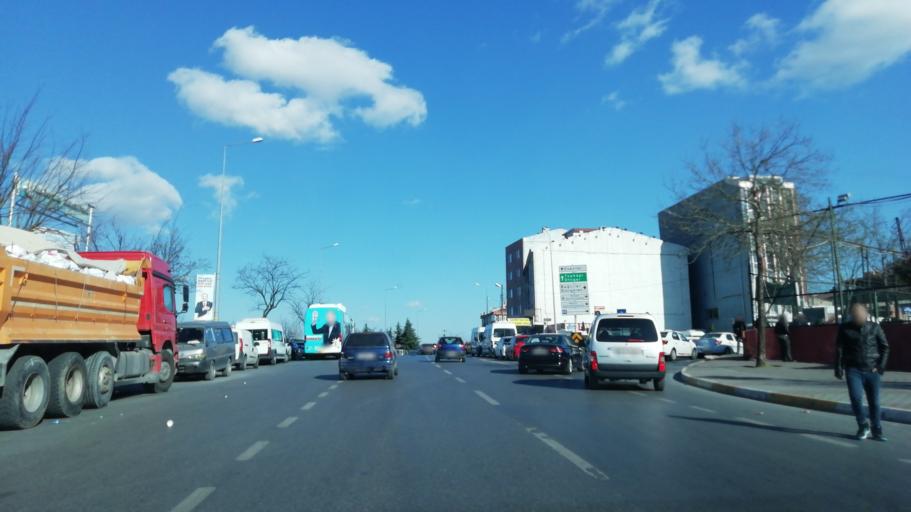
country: TR
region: Istanbul
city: Bagcilar
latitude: 41.0541
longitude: 28.8562
